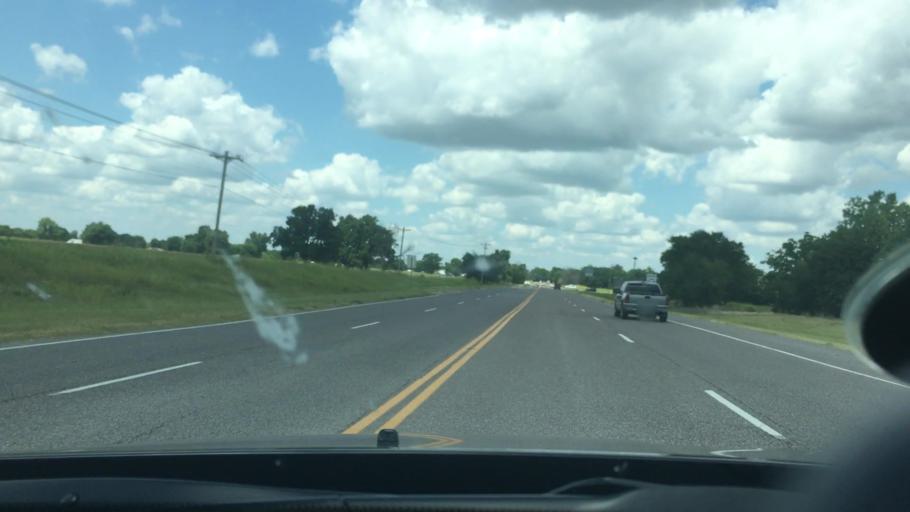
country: US
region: Oklahoma
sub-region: Murray County
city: Davis
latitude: 34.4643
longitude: -97.1306
